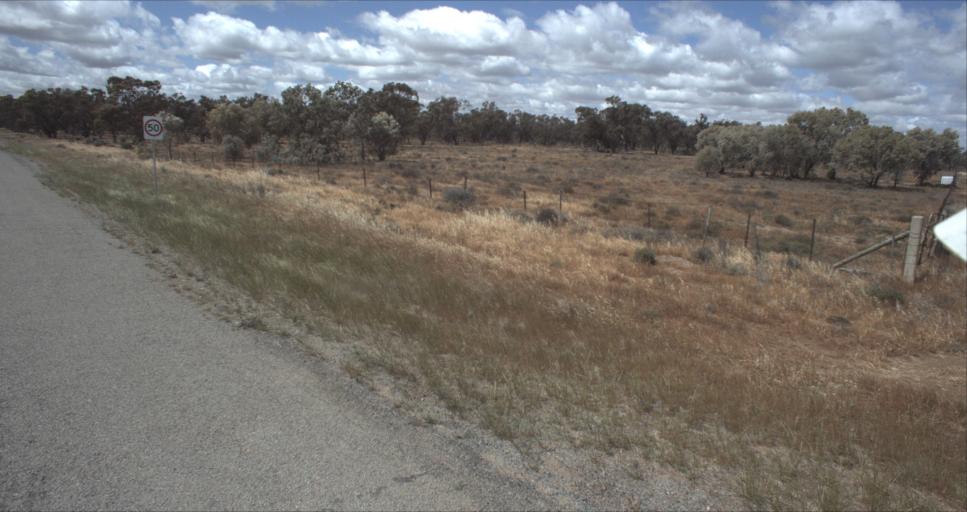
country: AU
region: New South Wales
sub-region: Murrumbidgee Shire
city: Darlington Point
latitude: -34.5191
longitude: 146.1764
